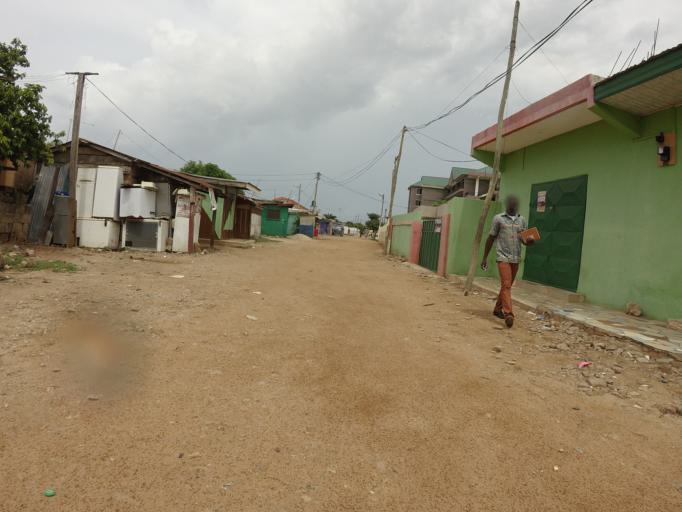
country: GH
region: Greater Accra
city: Accra
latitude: 5.6016
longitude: -0.2196
